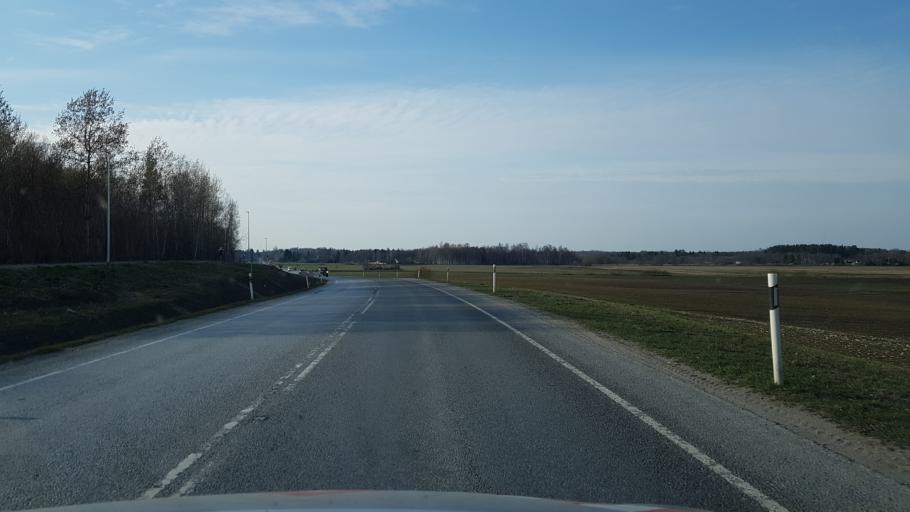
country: EE
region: Laeaene-Virumaa
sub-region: Rakvere linn
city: Rakvere
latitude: 59.3715
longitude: 26.3343
